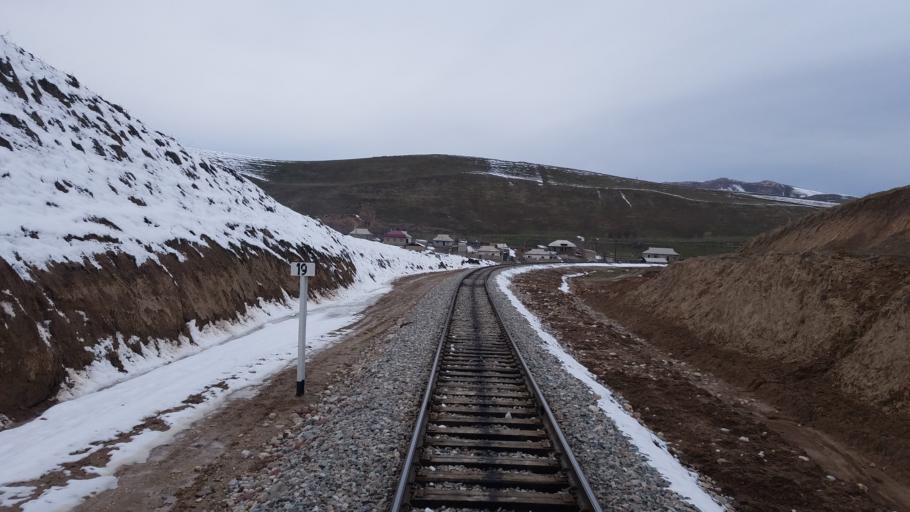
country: TJ
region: Khatlon
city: Yovon
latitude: 38.4254
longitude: 68.9541
